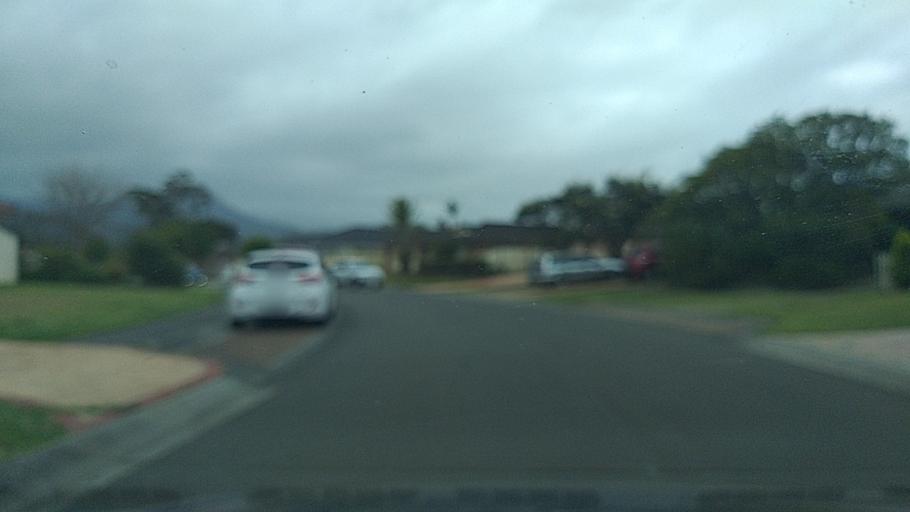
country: AU
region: New South Wales
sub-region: Wollongong
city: Dapto
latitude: -34.4885
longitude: 150.7737
